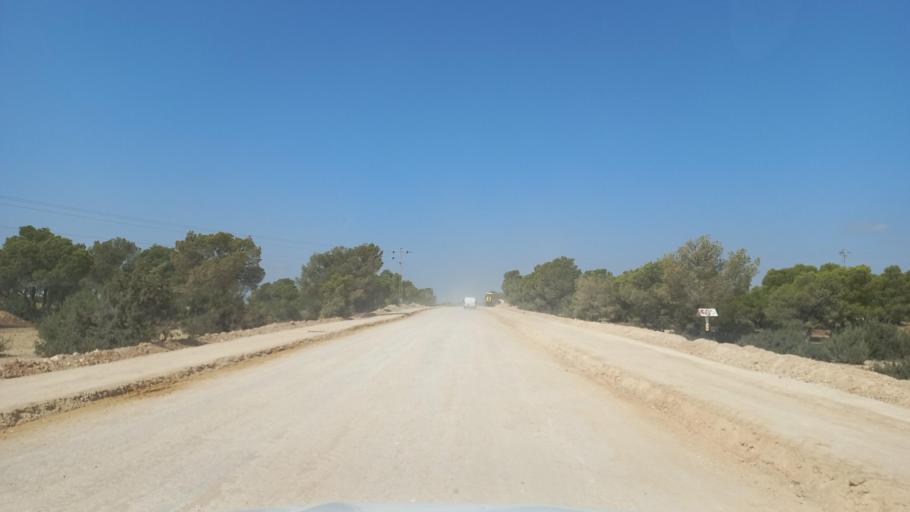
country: TN
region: Al Qasrayn
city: Sbiba
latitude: 35.4052
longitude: 8.9914
